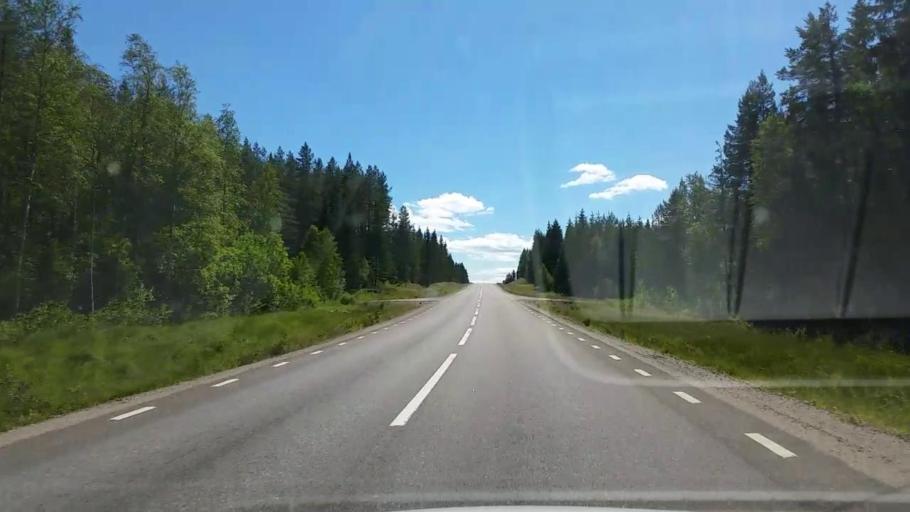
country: SE
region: Gaevleborg
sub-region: Ovanakers Kommun
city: Edsbyn
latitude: 61.0856
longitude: 15.8052
